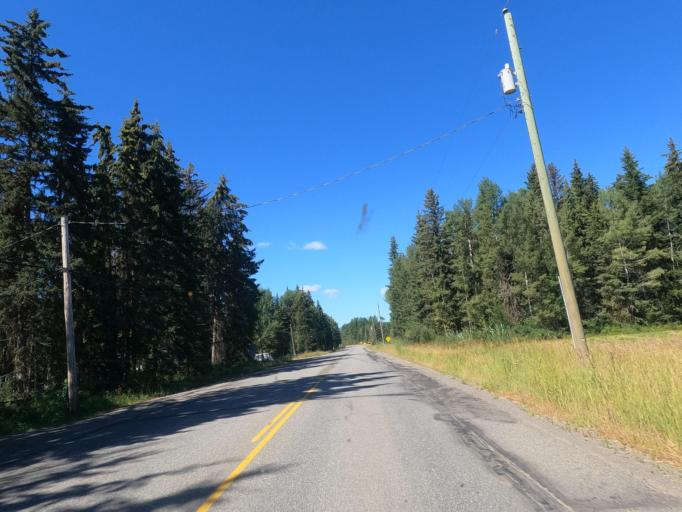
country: CA
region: British Columbia
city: Quesnel
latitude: 53.0197
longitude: -122.4658
